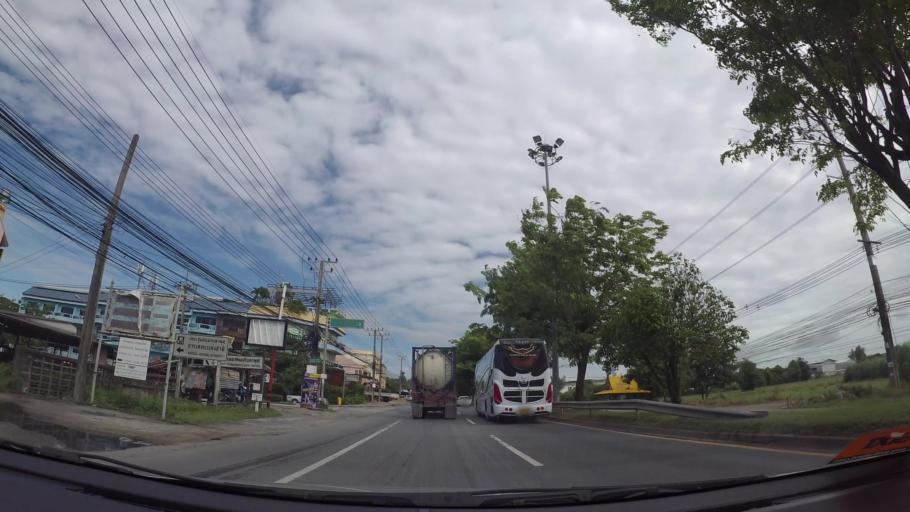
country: TH
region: Rayong
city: Ban Chang
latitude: 12.7354
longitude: 101.1305
